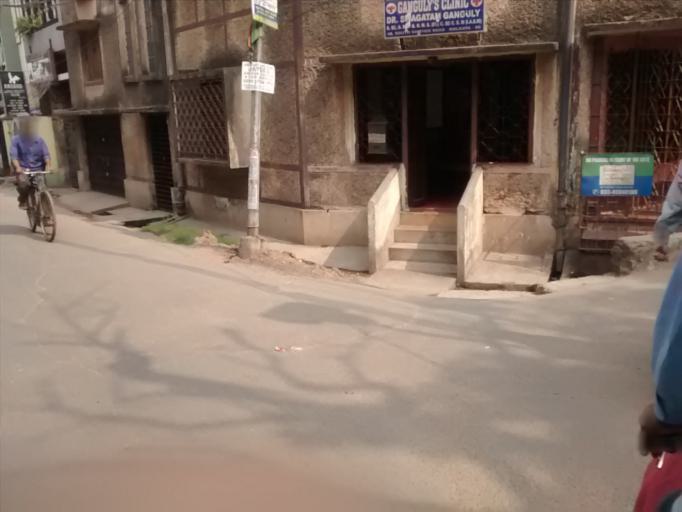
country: IN
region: West Bengal
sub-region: North 24 Parganas
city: Garui
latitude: 22.6244
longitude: 88.3892
